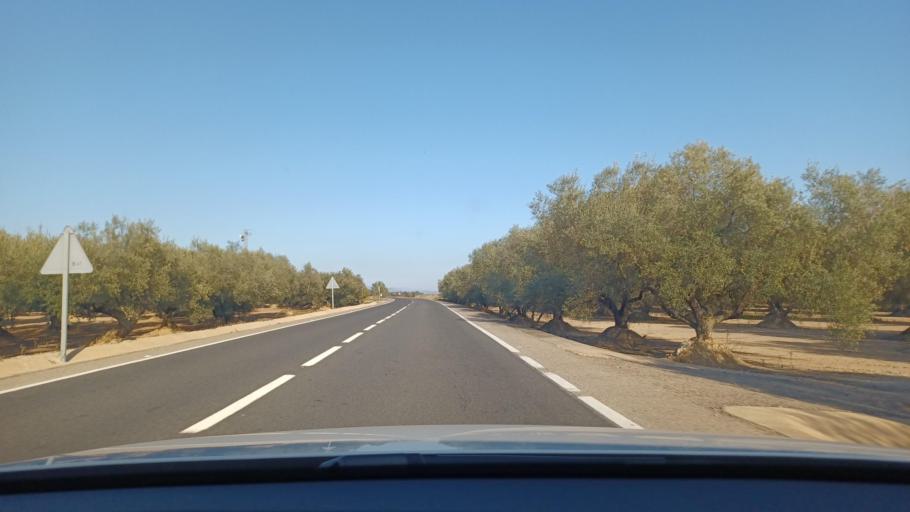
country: ES
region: Catalonia
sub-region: Provincia de Tarragona
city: Santa Barbara
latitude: 40.6701
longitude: 0.4405
